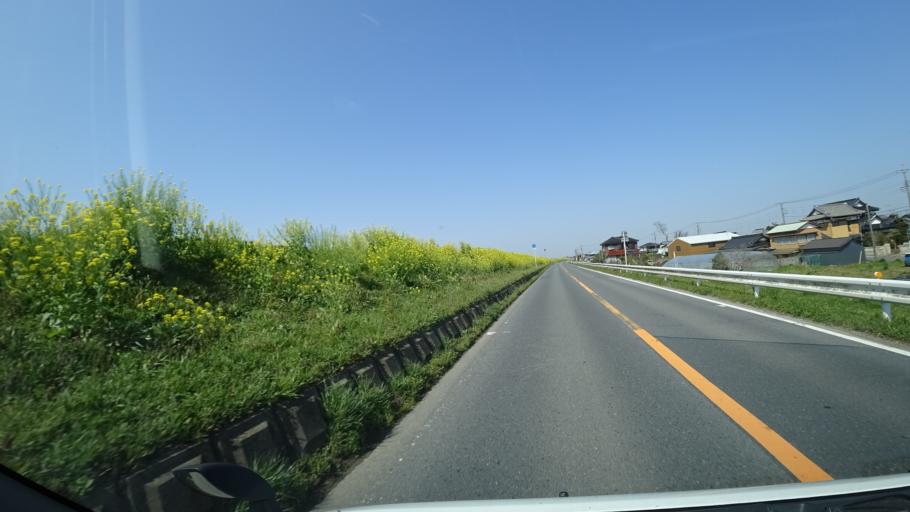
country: JP
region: Chiba
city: Katori-shi
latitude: 35.9100
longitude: 140.4156
